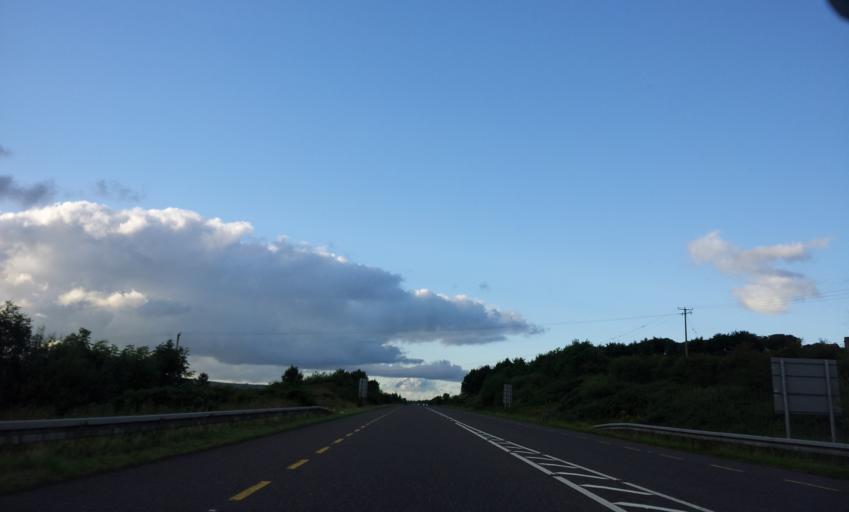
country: IE
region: Munster
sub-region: County Limerick
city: Abbeyfeale
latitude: 52.3195
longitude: -9.3595
